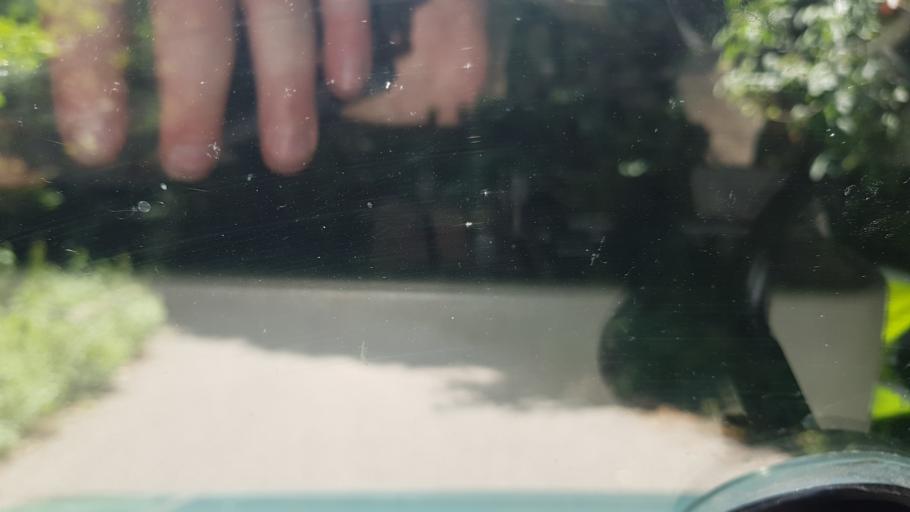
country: IT
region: Friuli Venezia Giulia
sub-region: Provincia di Udine
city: Lusevera
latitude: 46.2415
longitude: 13.2810
